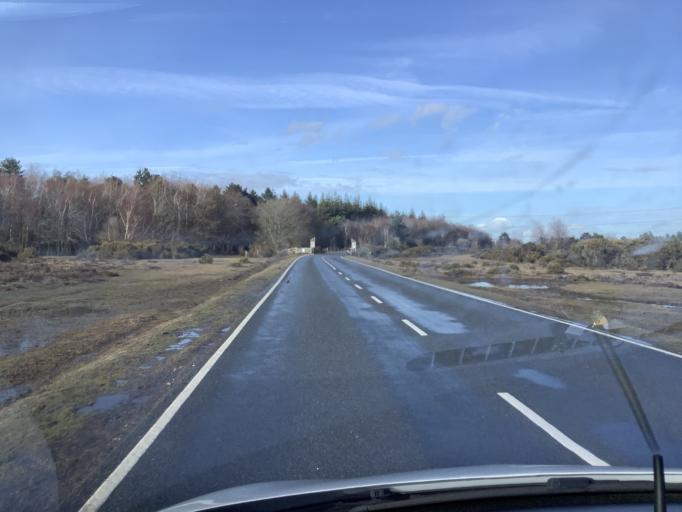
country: GB
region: England
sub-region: Hampshire
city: Hythe
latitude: 50.8464
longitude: -1.4237
